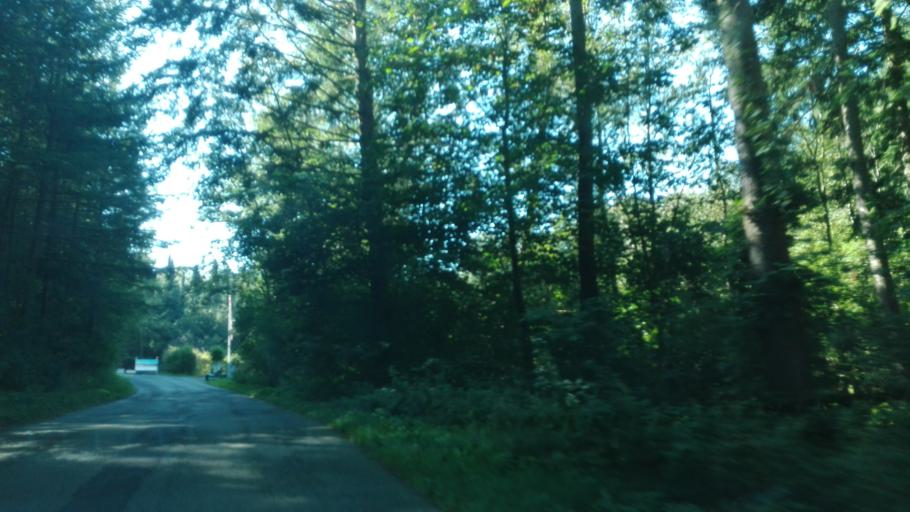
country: DK
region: Central Jutland
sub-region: Syddjurs Kommune
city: Ebeltoft
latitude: 56.2567
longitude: 10.6223
